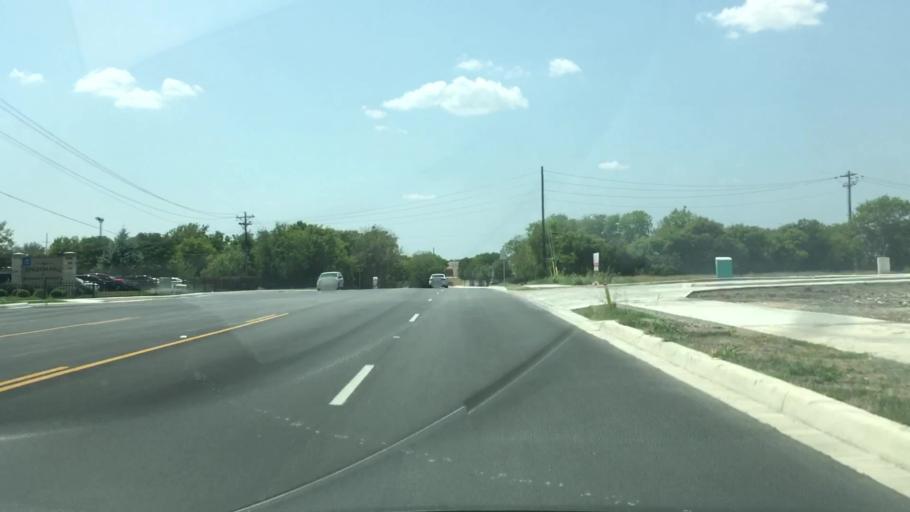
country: US
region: Texas
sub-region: Guadalupe County
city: Cibolo
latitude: 29.5693
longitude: -98.2452
